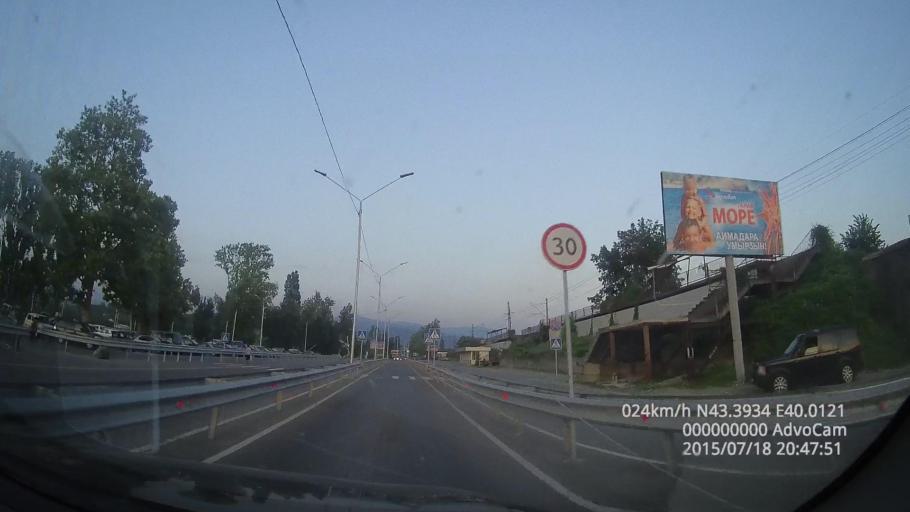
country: GE
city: Gantiadi
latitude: 43.3932
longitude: 40.0129
